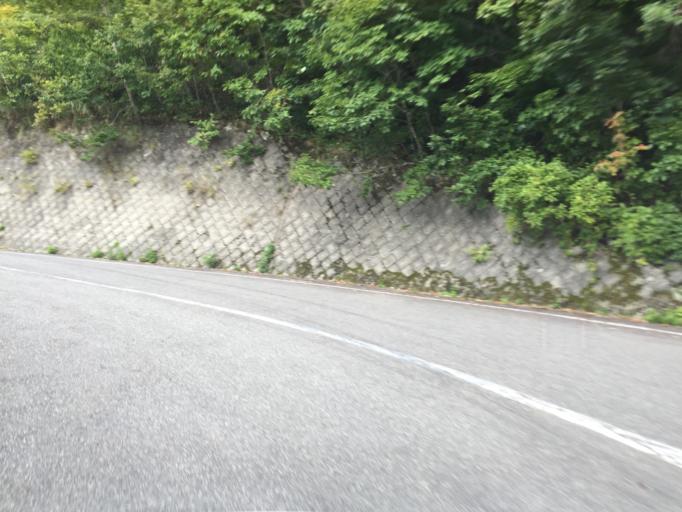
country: JP
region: Fukushima
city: Inawashiro
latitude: 37.6088
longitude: 140.0524
